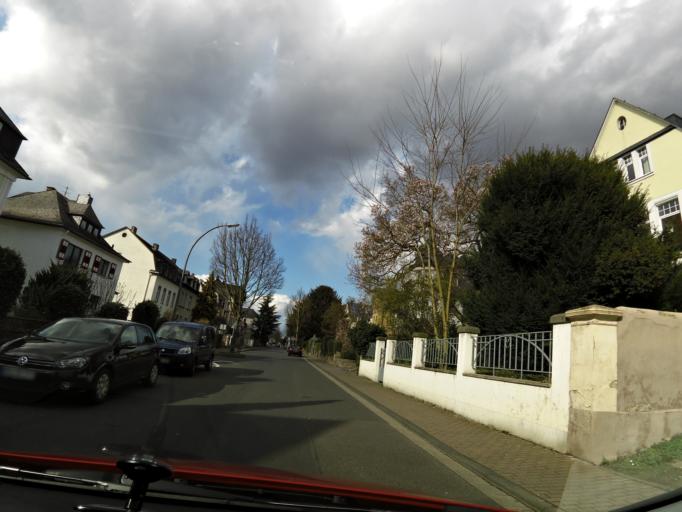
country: DE
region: Rheinland-Pfalz
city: Koblenz
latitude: 50.3343
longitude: 7.5988
